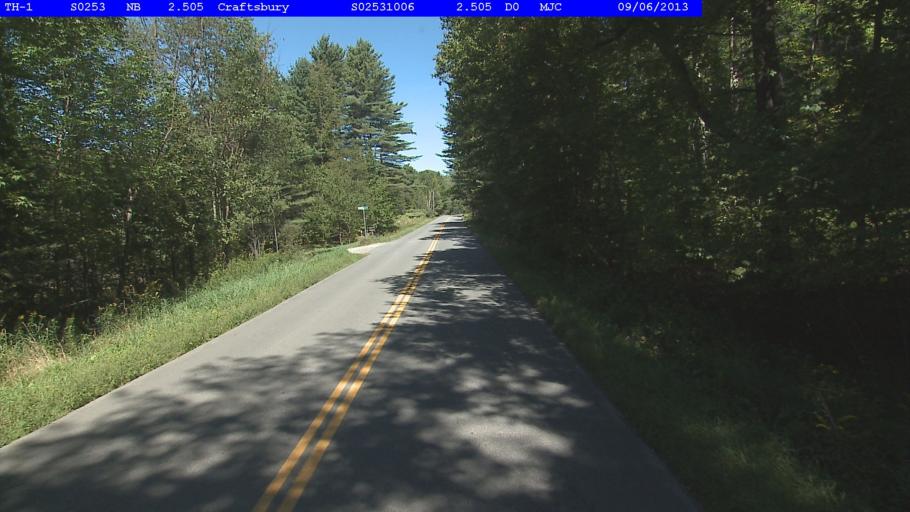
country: US
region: Vermont
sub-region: Caledonia County
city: Hardwick
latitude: 44.6444
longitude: -72.3793
